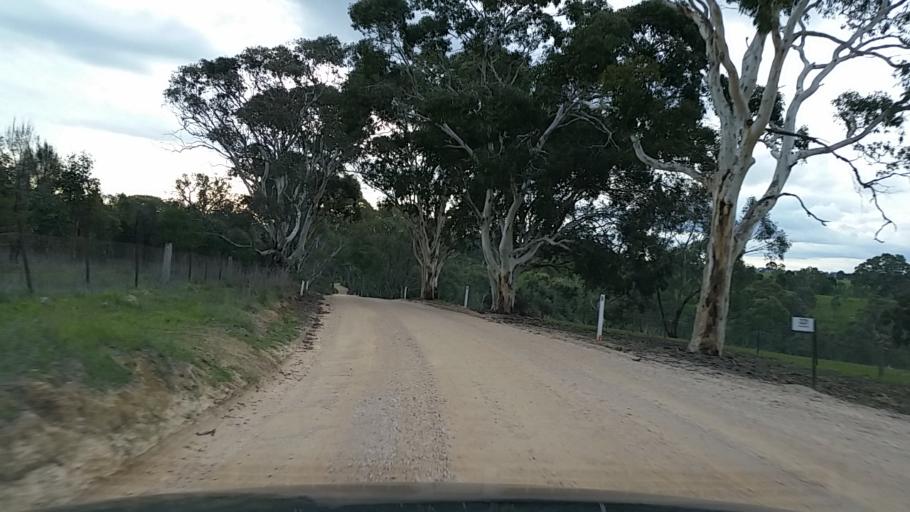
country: AU
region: South Australia
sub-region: Mount Barker
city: Nairne
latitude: -34.9683
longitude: 139.0268
